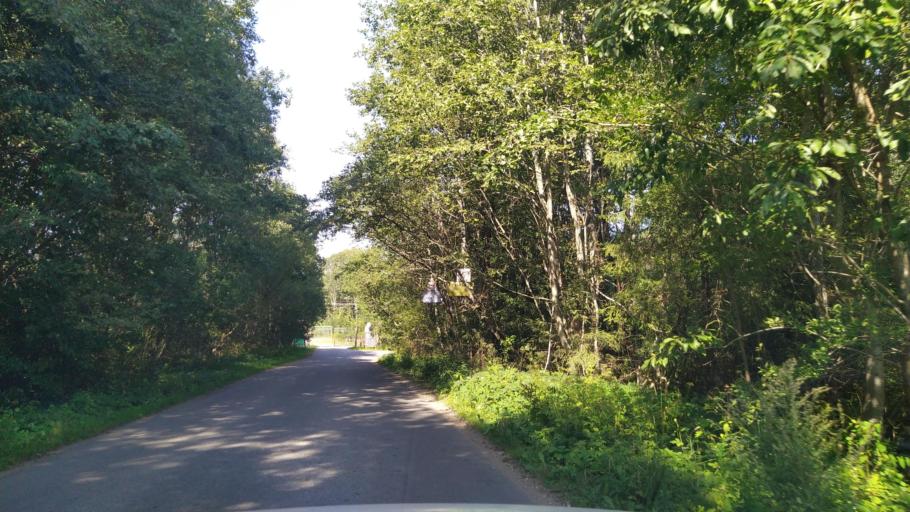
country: RU
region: Leningrad
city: Rozhdestveno
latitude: 59.2658
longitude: 30.0245
